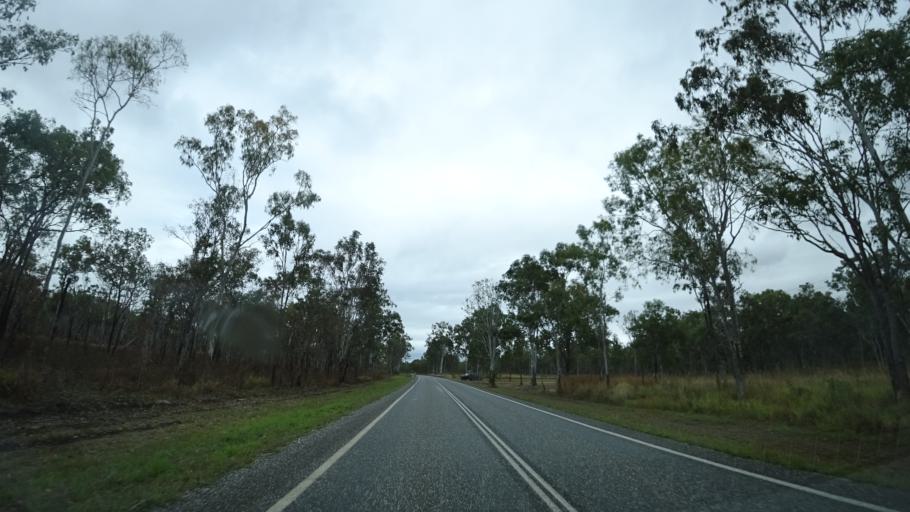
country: AU
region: Queensland
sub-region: Tablelands
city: Mareeba
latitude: -16.7469
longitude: 145.3446
